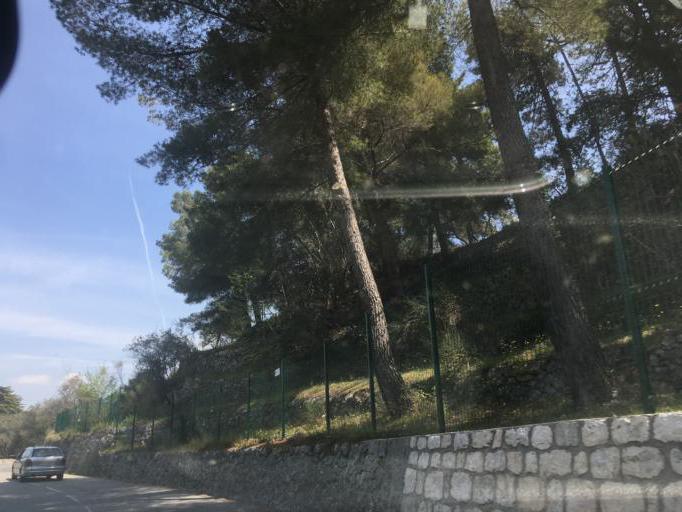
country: FR
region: Provence-Alpes-Cote d'Azur
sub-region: Departement des Alpes-Maritimes
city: Saint-Martin-du-Var
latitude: 43.8363
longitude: 7.2113
